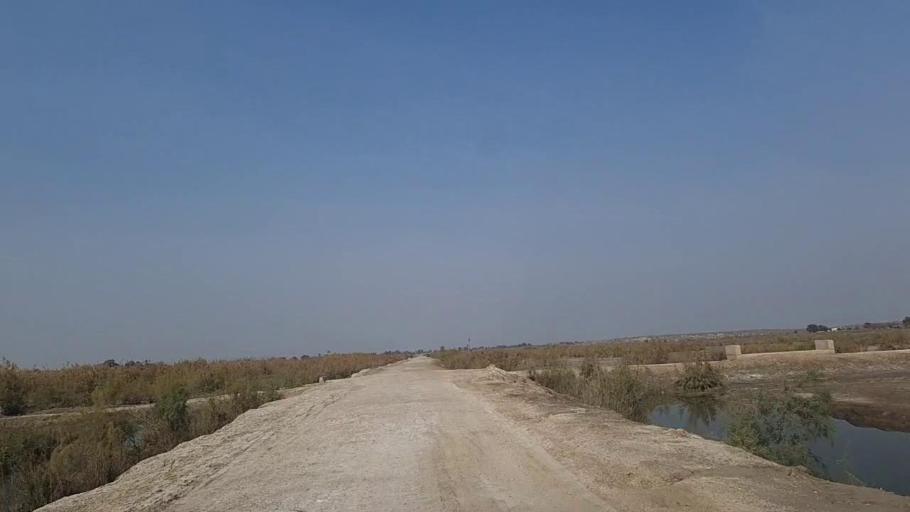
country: PK
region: Sindh
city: Daur
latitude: 26.5009
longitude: 68.4796
